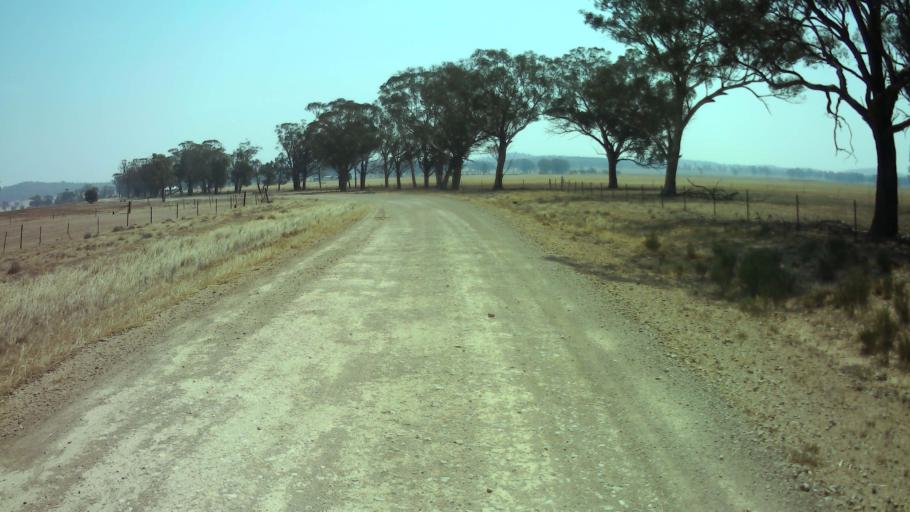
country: AU
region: New South Wales
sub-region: Weddin
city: Grenfell
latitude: -33.6390
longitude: 148.2486
